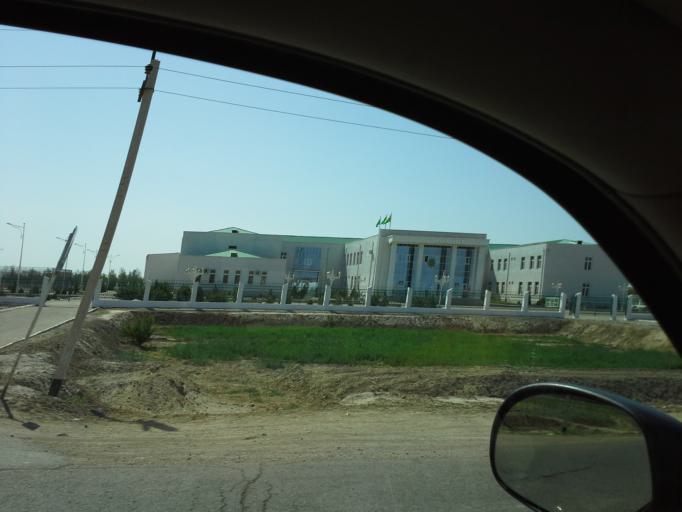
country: TM
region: Dasoguz
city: Dasoguz
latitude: 41.7982
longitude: 60.0171
